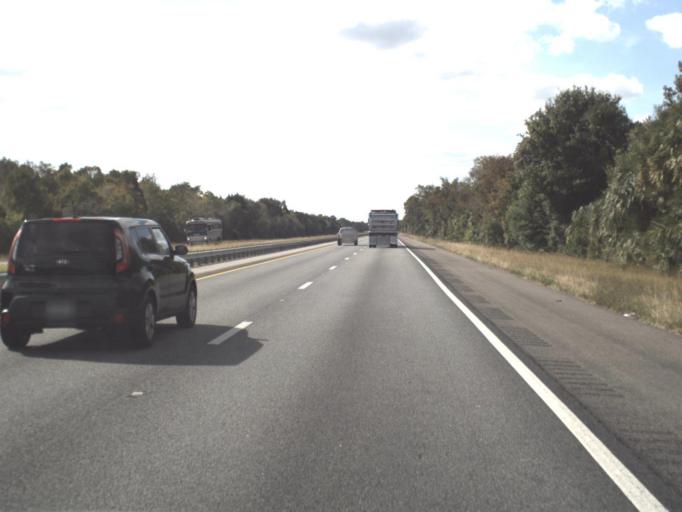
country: US
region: Florida
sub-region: Brevard County
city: Port Saint John
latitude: 28.4529
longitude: -80.9166
